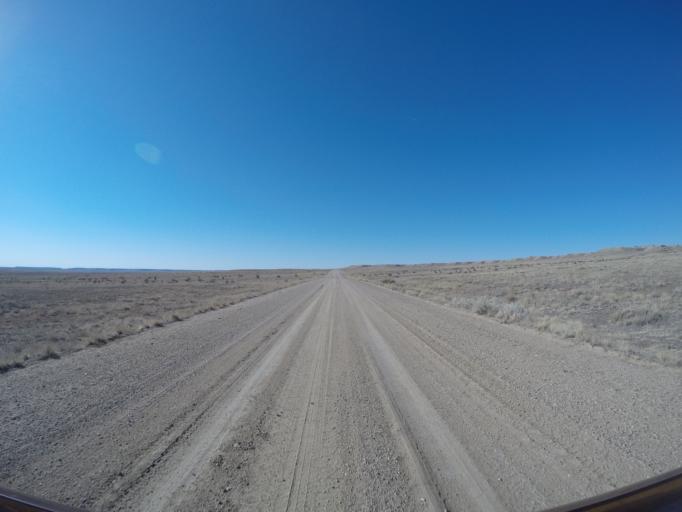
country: US
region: Colorado
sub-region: Otero County
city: La Junta
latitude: 37.7515
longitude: -103.6057
